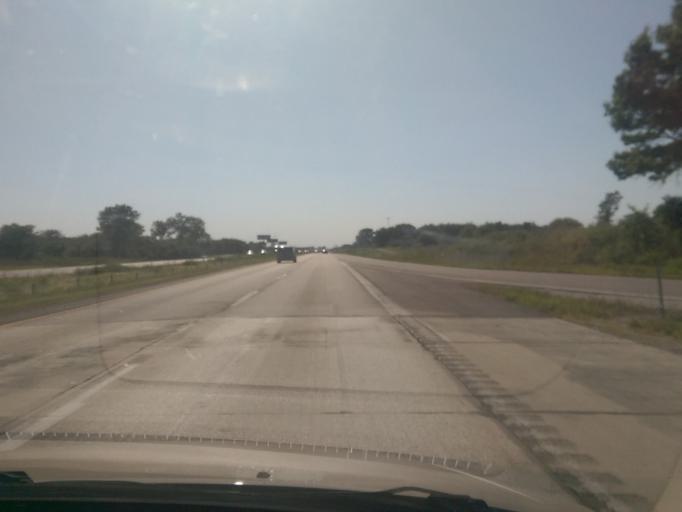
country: US
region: Missouri
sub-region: Saline County
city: Sweet Springs
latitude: 38.9737
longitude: -93.3332
